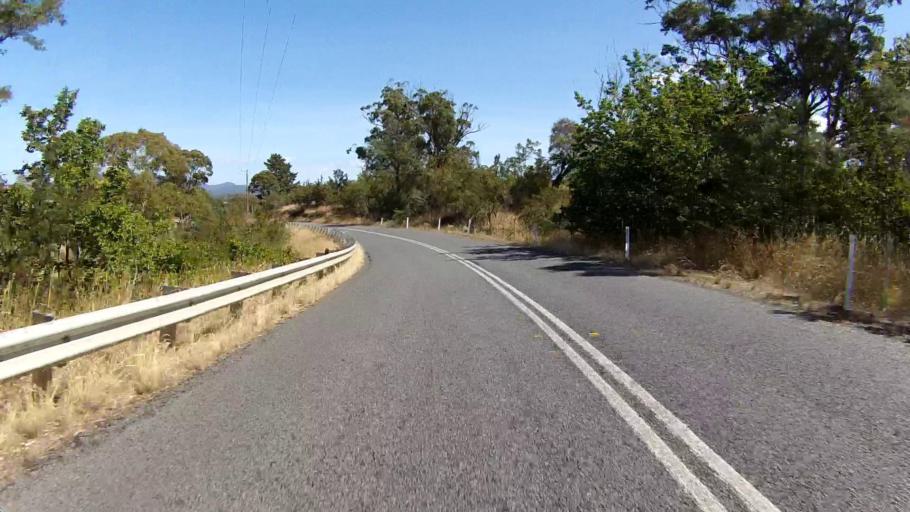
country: AU
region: Tasmania
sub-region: Sorell
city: Sorell
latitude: -42.4926
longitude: 147.9283
